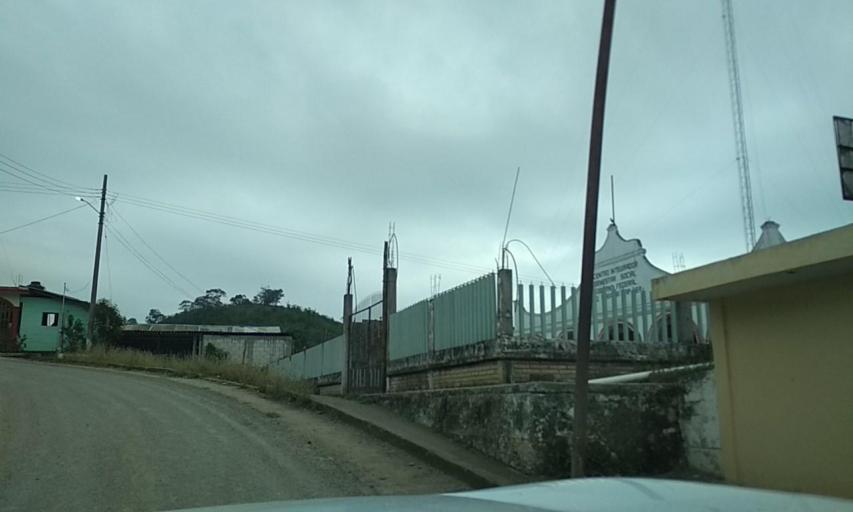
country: MX
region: Veracruz
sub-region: Coatzintla
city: Manuel Maria Contreras
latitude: 20.3595
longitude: -97.5110
